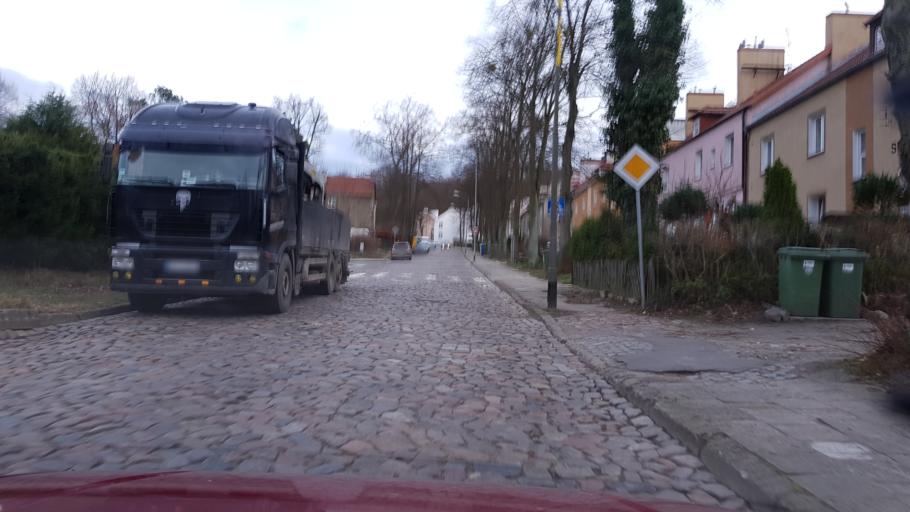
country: PL
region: West Pomeranian Voivodeship
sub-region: Szczecin
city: Szczecin
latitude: 53.3585
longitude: 14.5976
